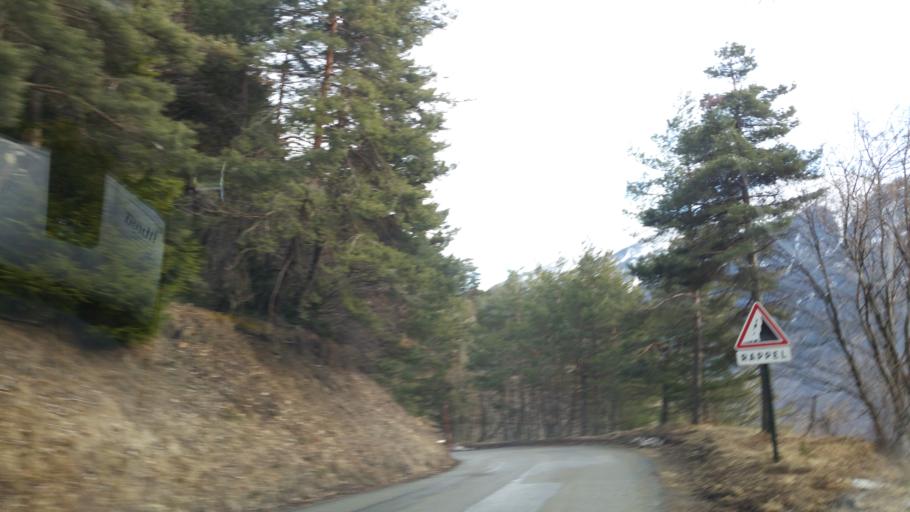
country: FR
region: Rhone-Alpes
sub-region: Departement de la Savoie
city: Villargondran
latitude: 45.2757
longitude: 6.3856
